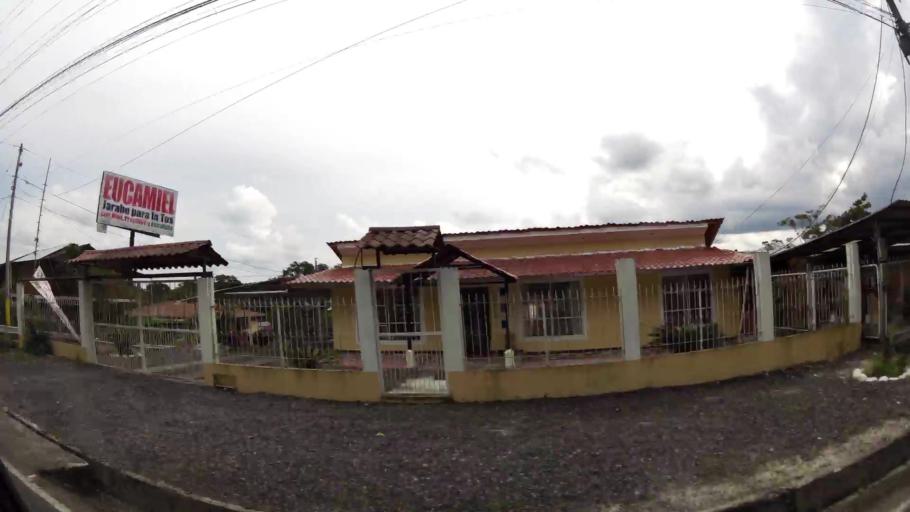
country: EC
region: Pastaza
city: Puyo
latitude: -1.5055
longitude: -78.0412
